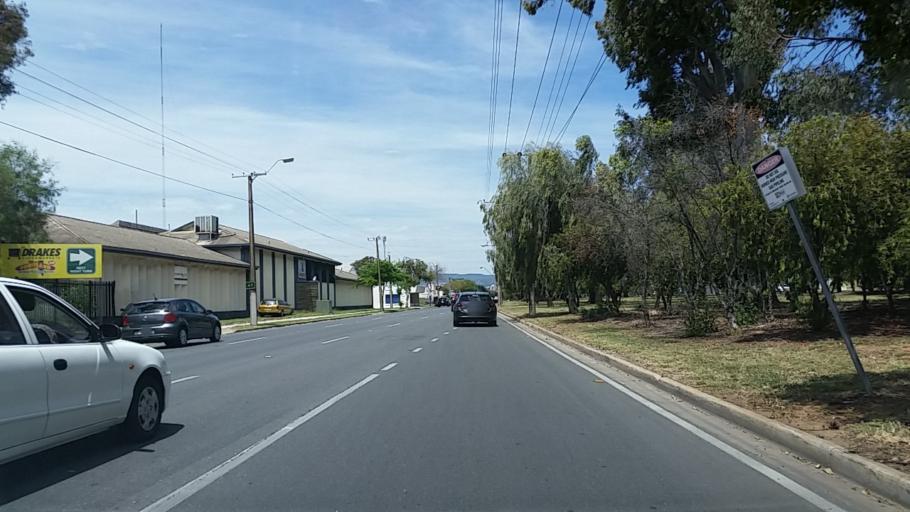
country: AU
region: South Australia
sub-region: Charles Sturt
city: Allenby Gardens
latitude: -34.8916
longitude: 138.5518
